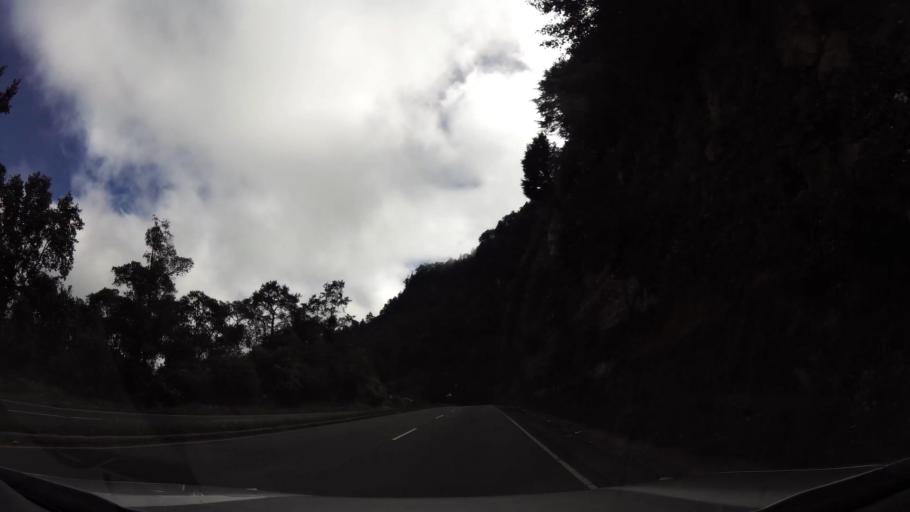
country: GT
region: Solola
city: Santa Catarina Ixtahuacan
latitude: 14.8419
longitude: -91.3870
